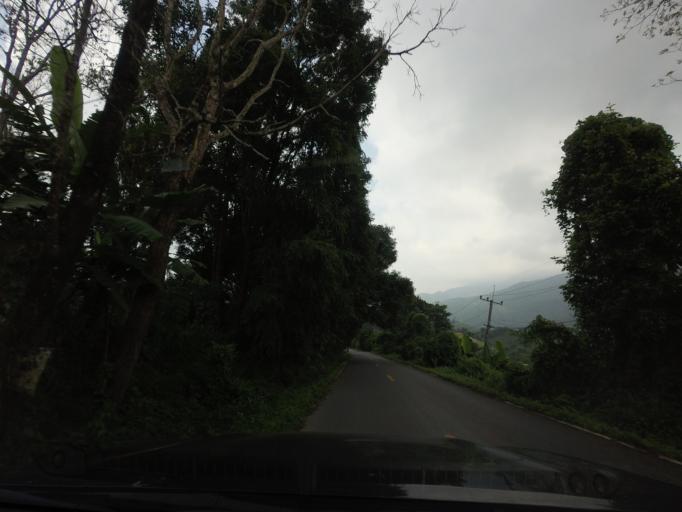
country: TH
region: Nan
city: Bo Kluea
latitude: 19.1932
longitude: 101.0461
